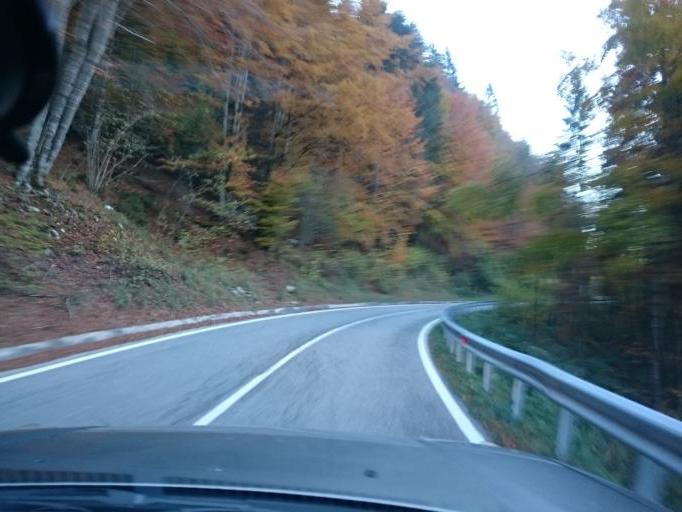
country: IT
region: Veneto
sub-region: Provincia di Vicenza
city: Roana
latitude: 45.9044
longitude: 11.4607
